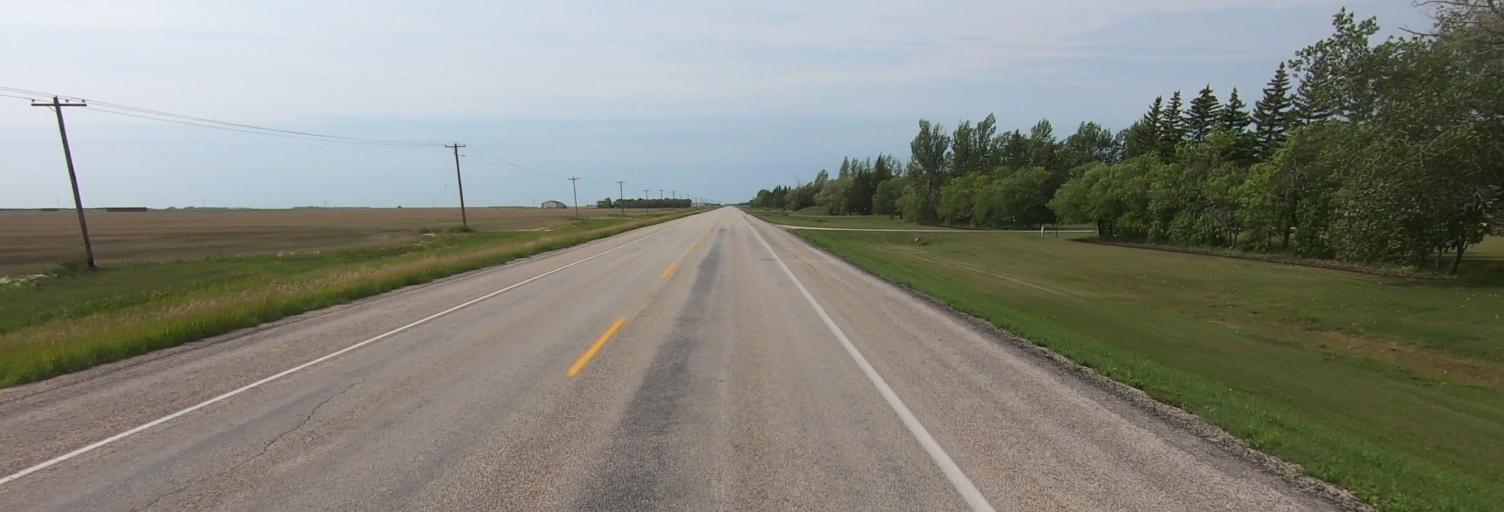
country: CA
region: Manitoba
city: Niverville
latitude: 49.5781
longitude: -97.1483
